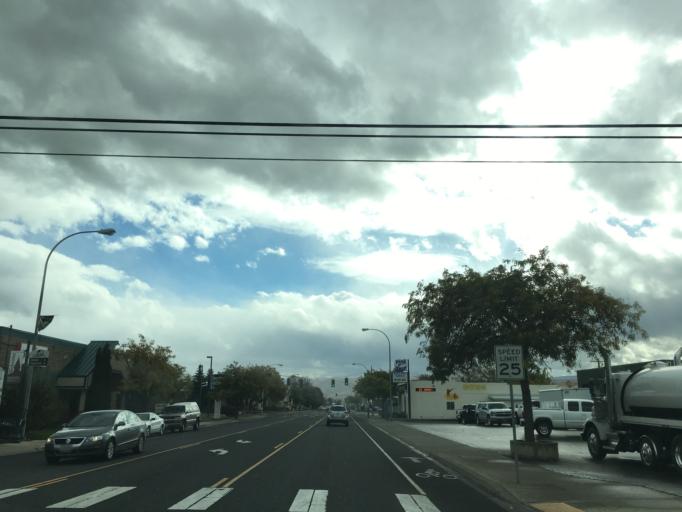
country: US
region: Washington
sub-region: Kittitas County
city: Ellensburg
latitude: 46.9934
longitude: -120.5486
